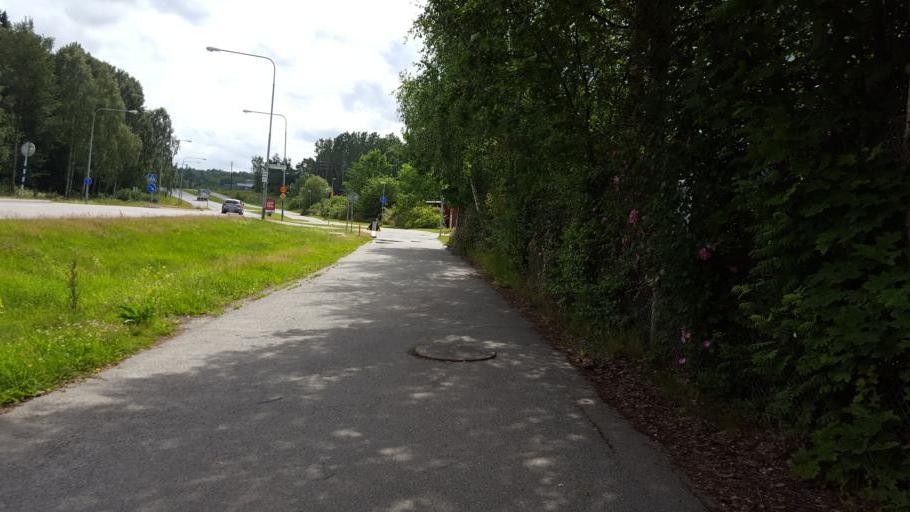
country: SE
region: Stockholm
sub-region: Upplands Vasby Kommun
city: Upplands Vaesby
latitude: 59.5143
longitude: 17.8988
